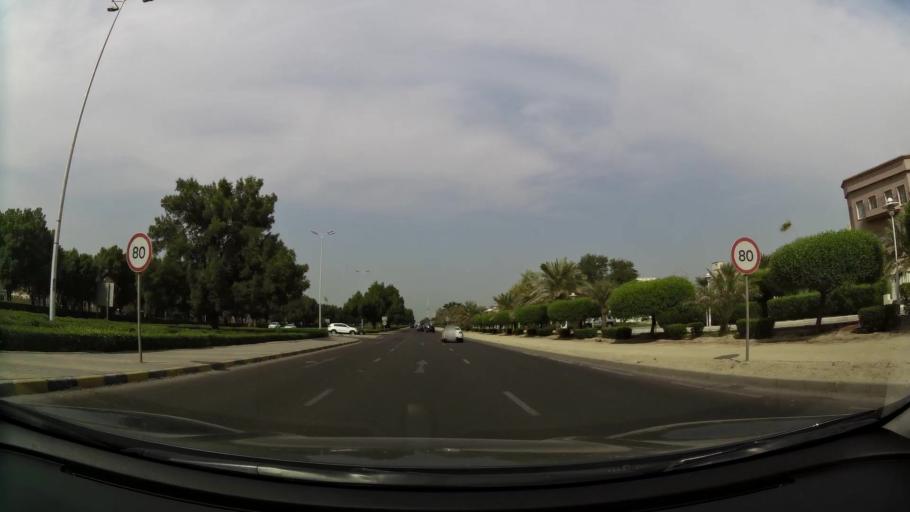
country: KW
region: Muhafazat Hawalli
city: Hawalli
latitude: 29.3243
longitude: 47.9920
